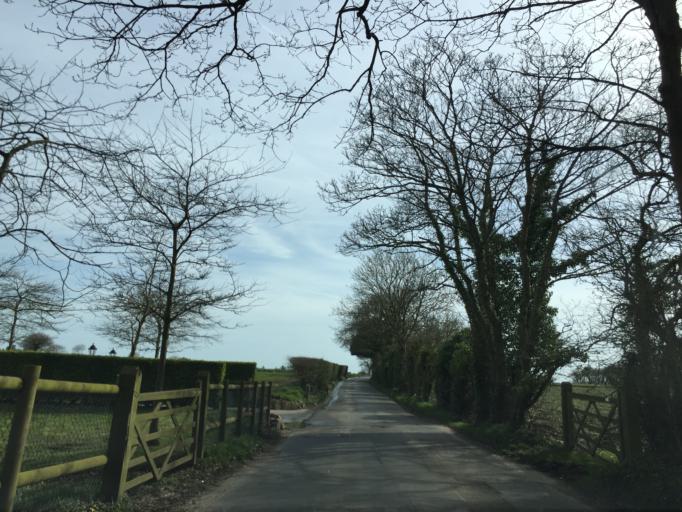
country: JE
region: St Helier
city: Saint Helier
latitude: 49.2296
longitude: -2.1104
